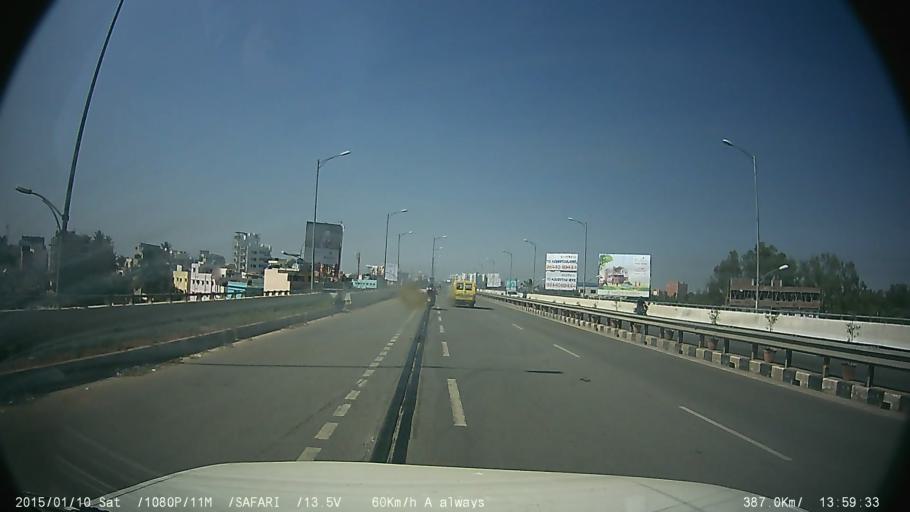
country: IN
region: Karnataka
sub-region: Bangalore Urban
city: Bangalore
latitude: 12.8522
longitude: 77.6672
